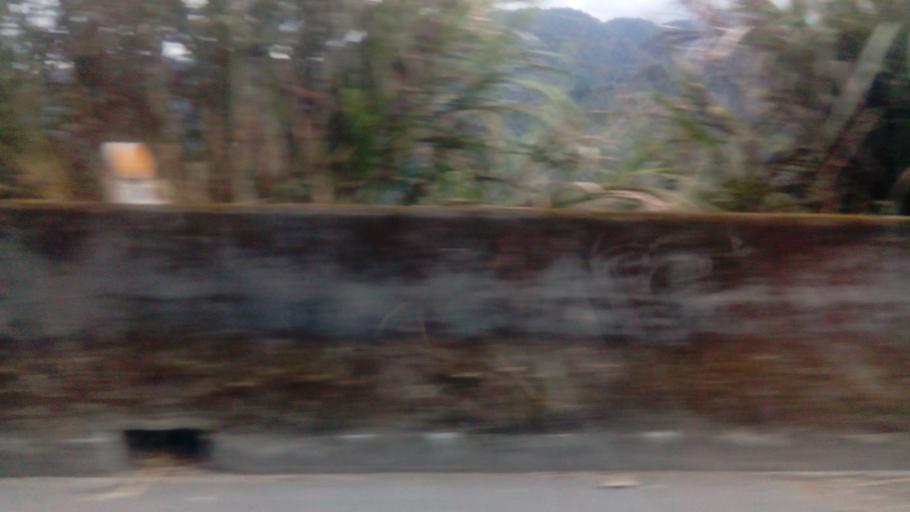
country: TW
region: Taiwan
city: Daxi
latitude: 24.4604
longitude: 121.3945
